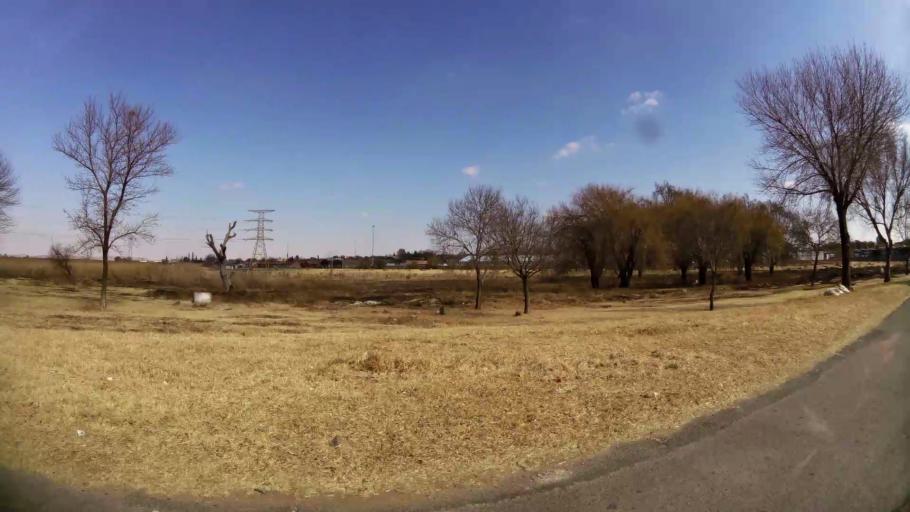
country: ZA
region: Gauteng
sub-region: City of Johannesburg Metropolitan Municipality
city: Soweto
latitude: -26.2651
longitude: 27.8827
